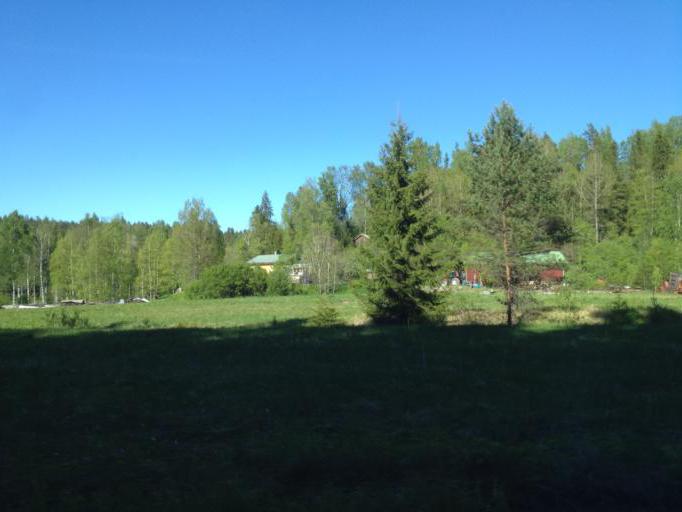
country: FI
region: Uusimaa
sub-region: Helsinki
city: Espoo
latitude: 60.3083
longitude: 24.5290
